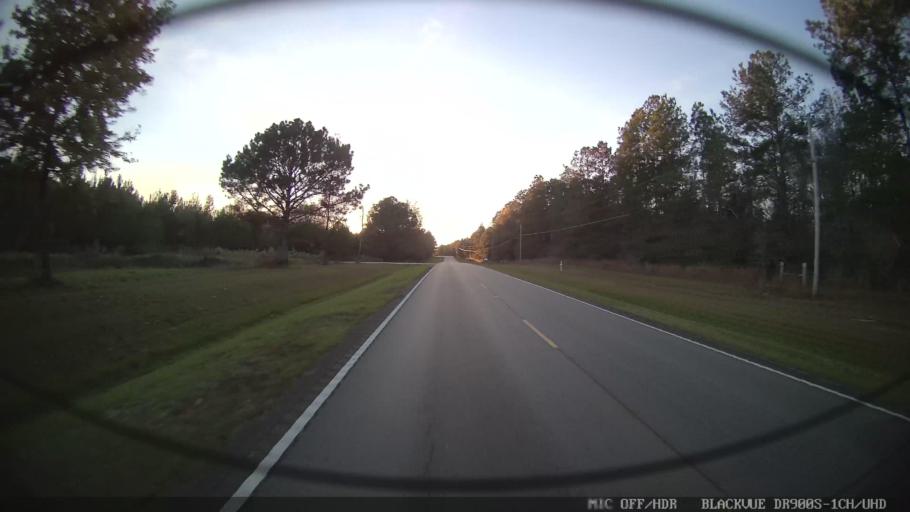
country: US
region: Mississippi
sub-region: Stone County
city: Wiggins
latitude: 31.0311
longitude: -89.2280
